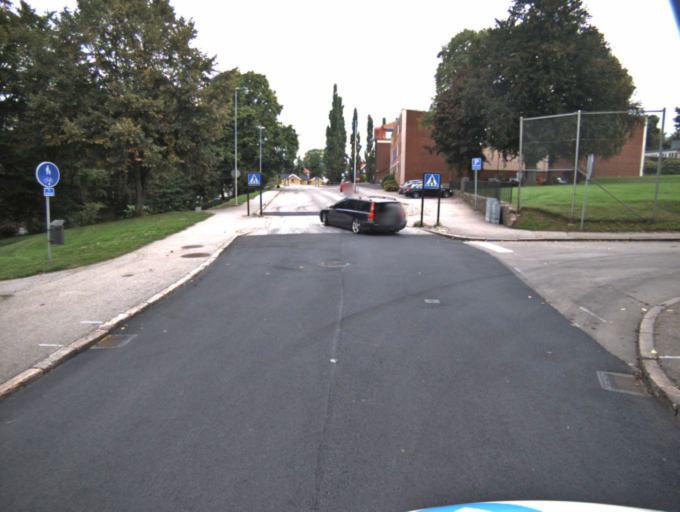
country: SE
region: Vaestra Goetaland
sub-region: Ulricehamns Kommun
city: Ulricehamn
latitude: 57.7886
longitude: 13.4157
